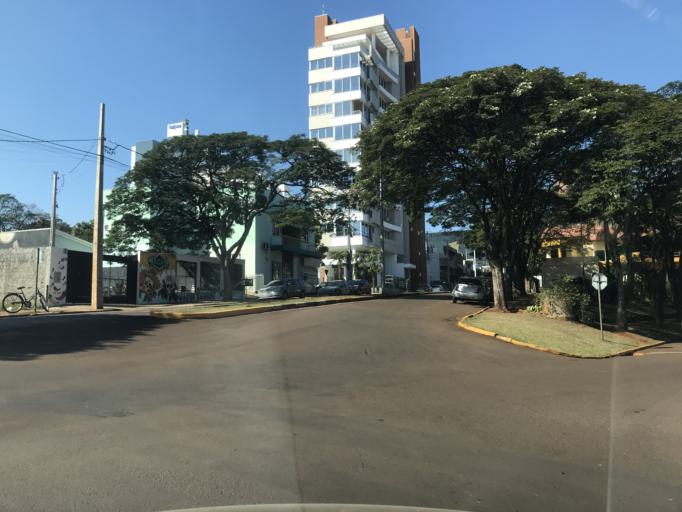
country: BR
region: Parana
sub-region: Toledo
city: Toledo
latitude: -24.7241
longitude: -53.7432
